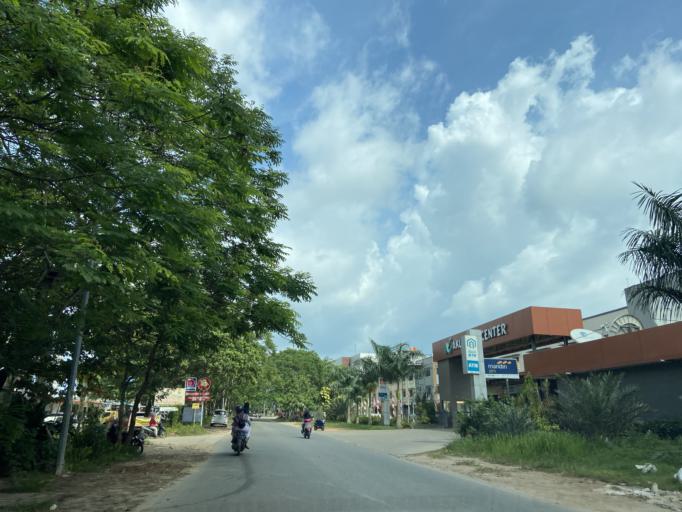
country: SG
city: Singapore
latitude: 1.1343
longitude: 104.0343
